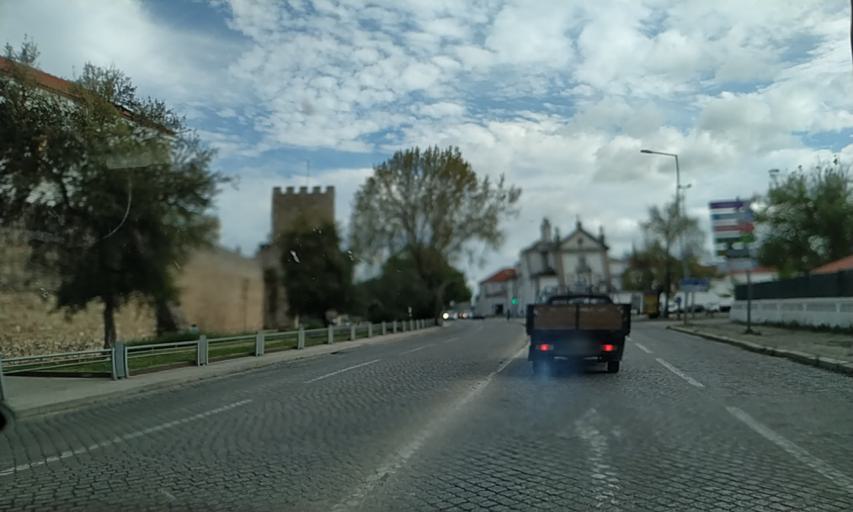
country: PT
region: Evora
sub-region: Evora
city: Evora
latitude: 38.5712
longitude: -7.9152
